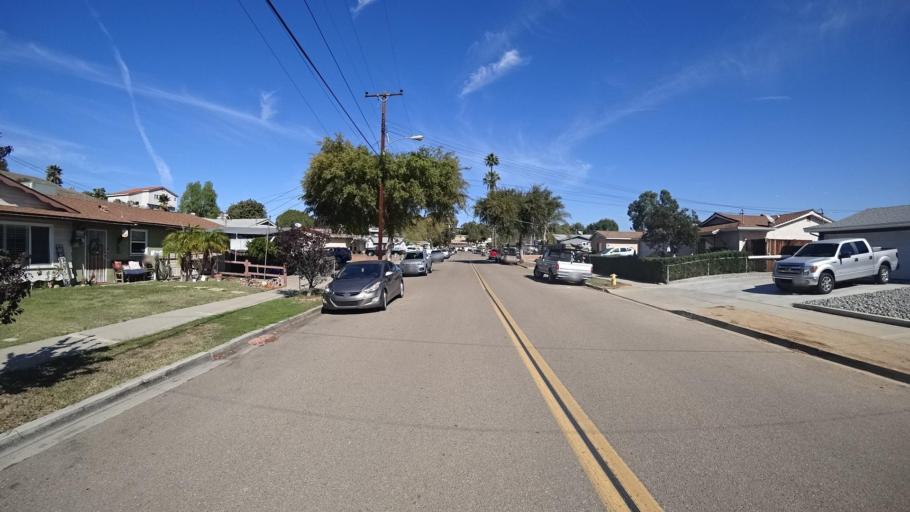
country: US
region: California
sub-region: San Diego County
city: Lemon Grove
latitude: 32.7232
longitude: -117.0220
